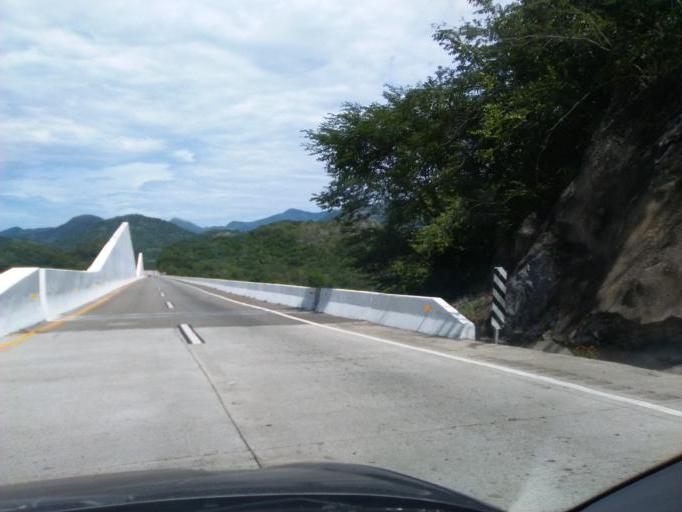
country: MX
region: Guerrero
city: Tierra Colorada
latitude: 17.1300
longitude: -99.5594
